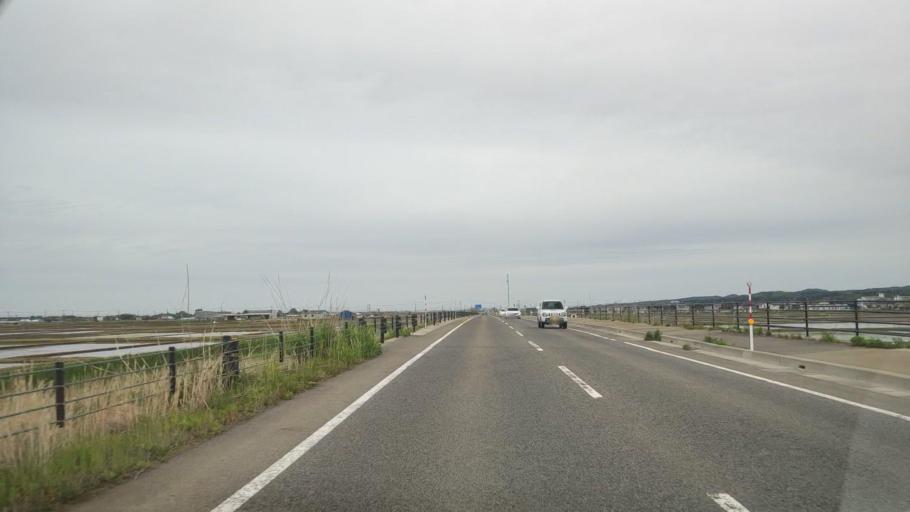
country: JP
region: Niigata
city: Shirone
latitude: 37.7463
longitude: 139.0841
